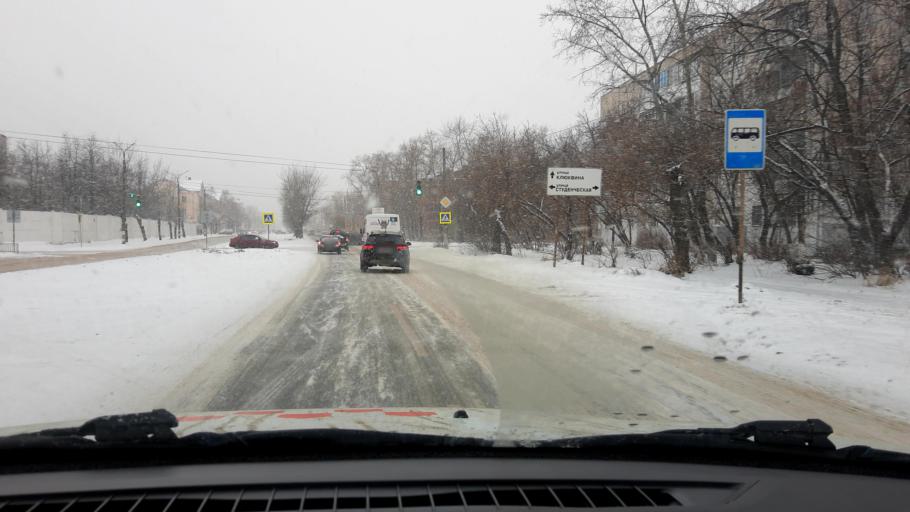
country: RU
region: Nizjnij Novgorod
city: Dzerzhinsk
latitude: 56.2402
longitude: 43.4903
